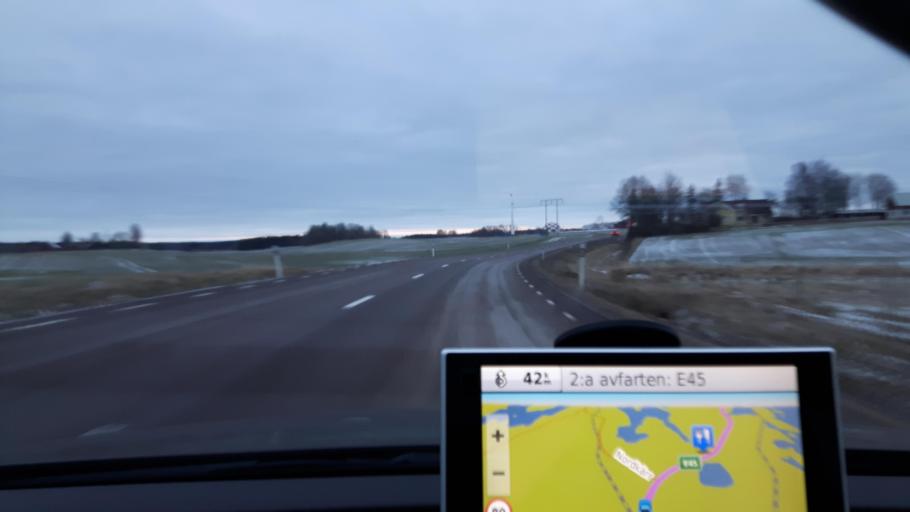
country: SE
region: Vaestra Goetaland
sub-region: Melleruds Kommun
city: Mellerud
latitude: 58.7250
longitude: 12.4529
